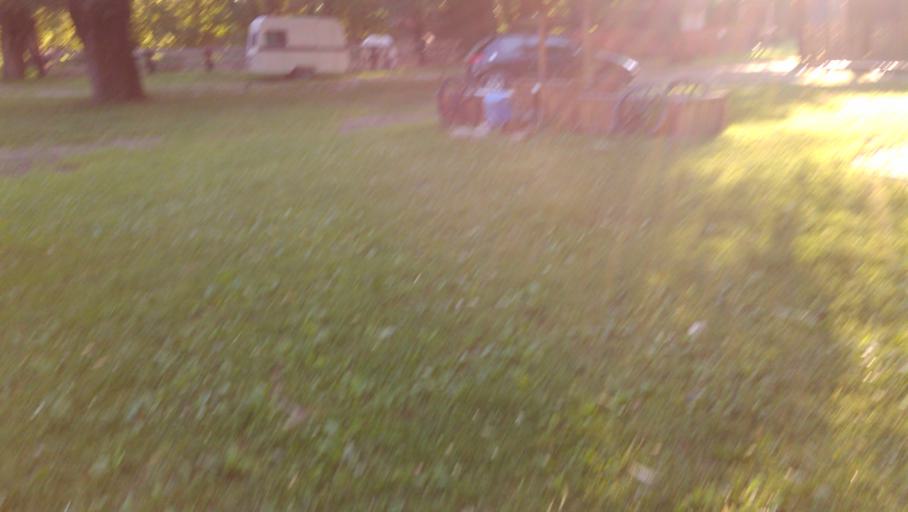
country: SK
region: Nitriansky
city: Kolarovo
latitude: 47.9206
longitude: 18.0031
